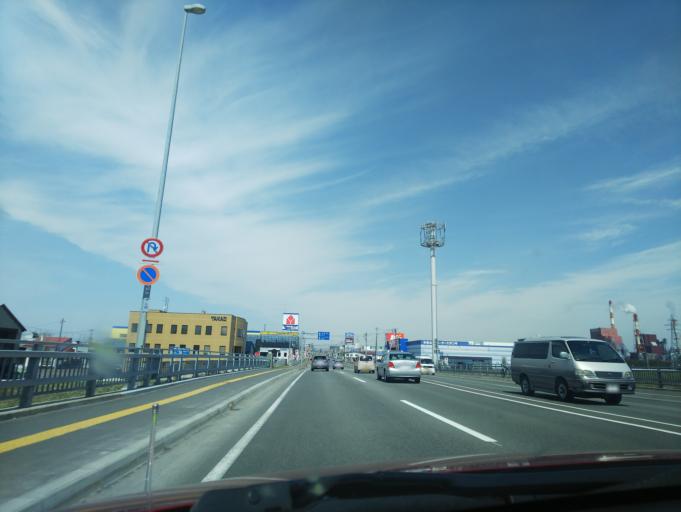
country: JP
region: Hokkaido
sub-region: Asahikawa-shi
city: Asahikawa
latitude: 43.7720
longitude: 142.3819
